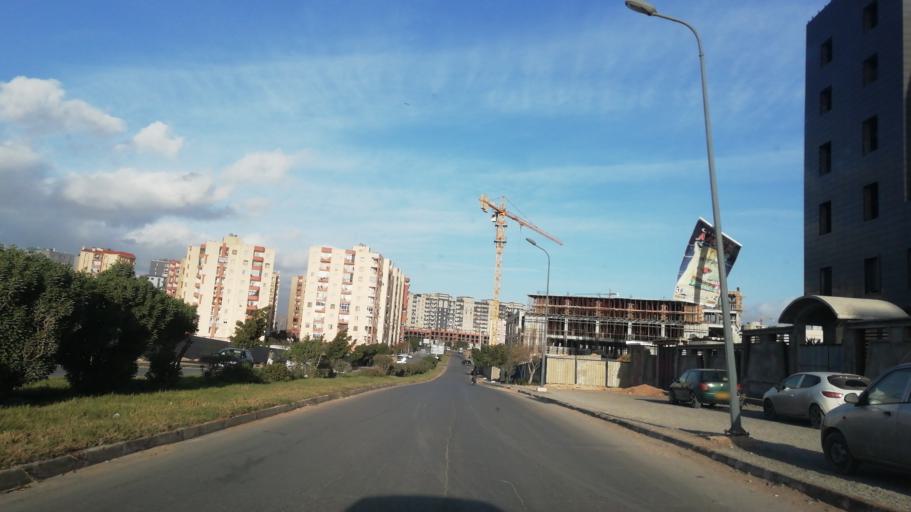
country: DZ
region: Oran
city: Bir el Djir
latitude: 35.7074
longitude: -0.5700
